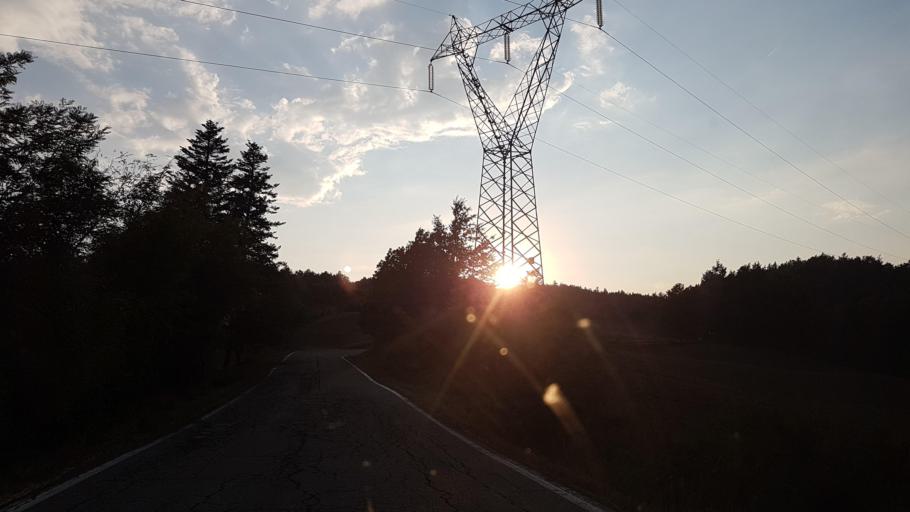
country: IT
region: Emilia-Romagna
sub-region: Provincia di Parma
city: Albareto
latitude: 44.4585
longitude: 9.6851
